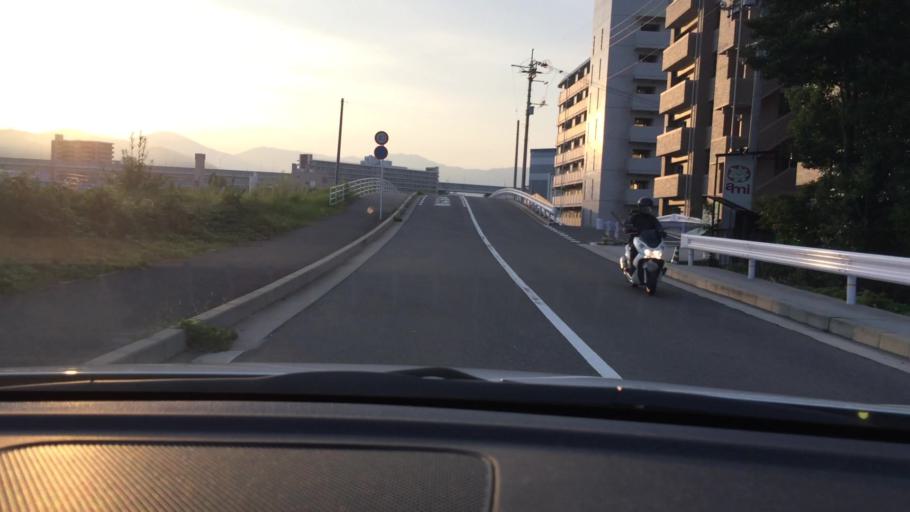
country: JP
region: Hiroshima
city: Hiroshima-shi
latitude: 34.3845
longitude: 132.4924
